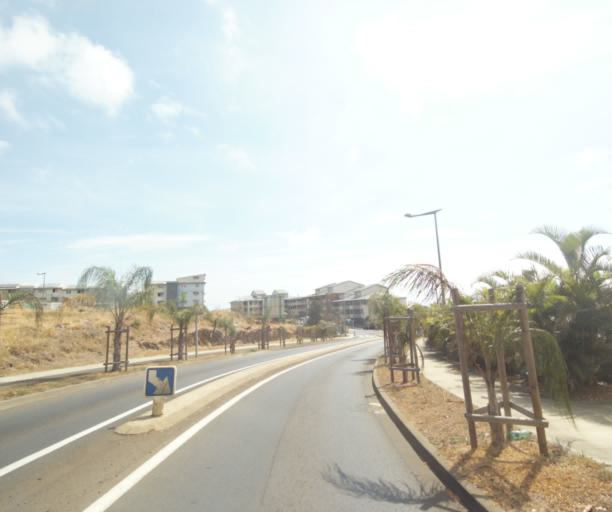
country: RE
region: Reunion
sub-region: Reunion
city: Saint-Paul
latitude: -21.0455
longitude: 55.2608
